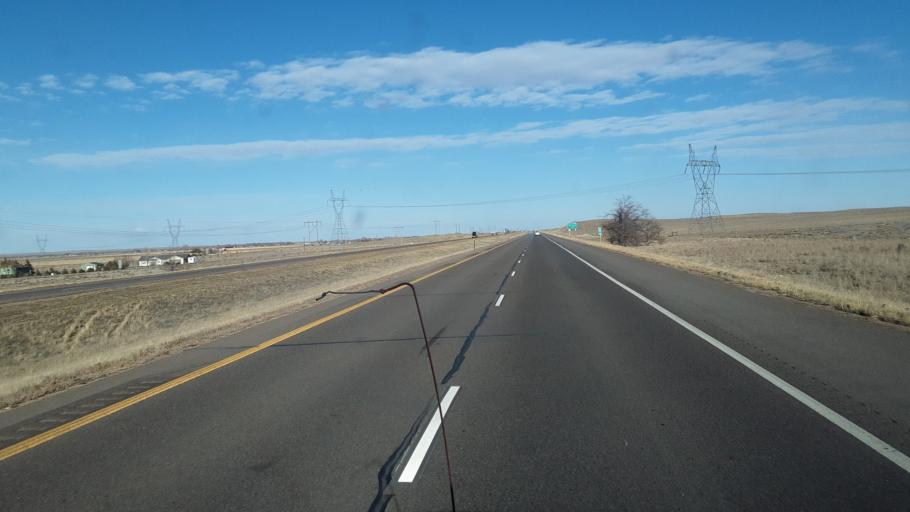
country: US
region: Colorado
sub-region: Morgan County
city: Brush
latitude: 40.2887
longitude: -103.5489
